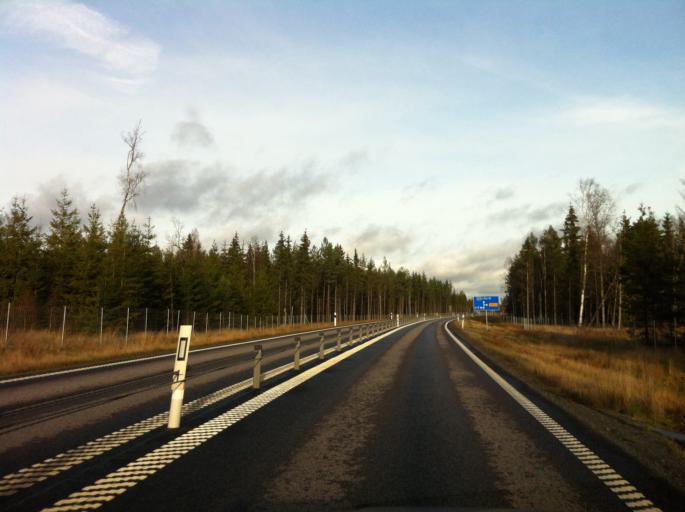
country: SE
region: Kronoberg
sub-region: Almhults Kommun
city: AElmhult
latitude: 56.6426
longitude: 14.2706
